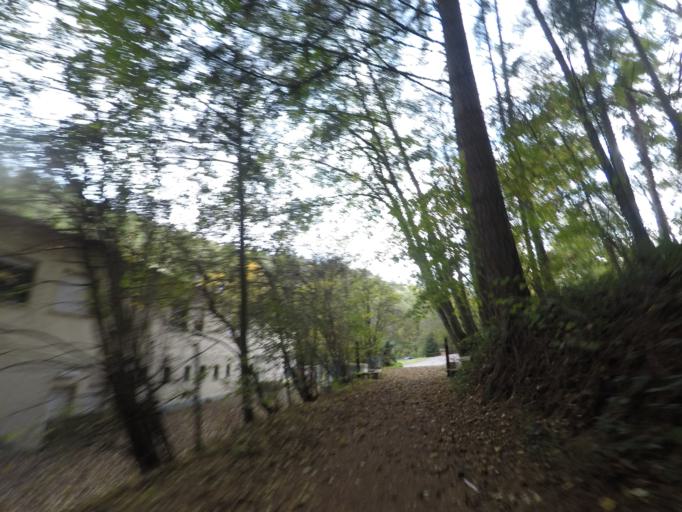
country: LU
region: Luxembourg
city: Itzig
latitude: 49.5960
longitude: 6.1603
